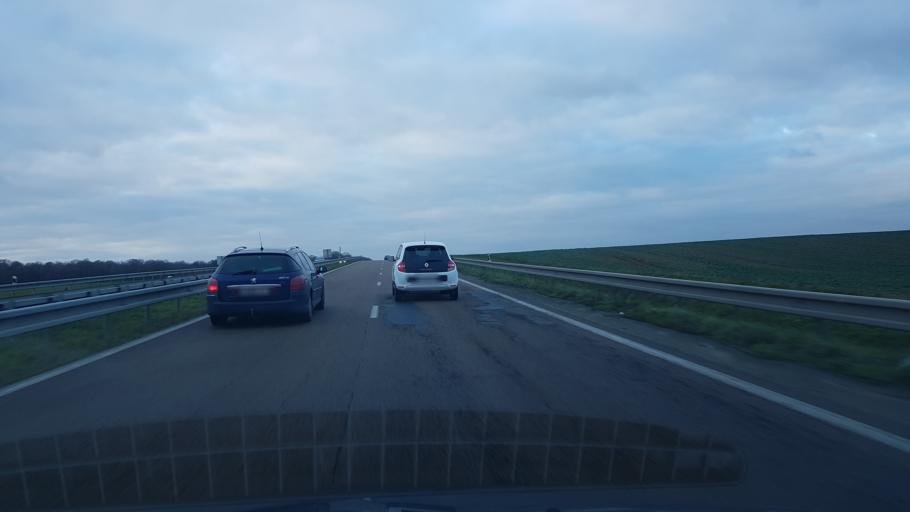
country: FR
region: Champagne-Ardenne
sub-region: Departement de la Marne
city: Sezanne
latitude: 48.7285
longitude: 3.6661
